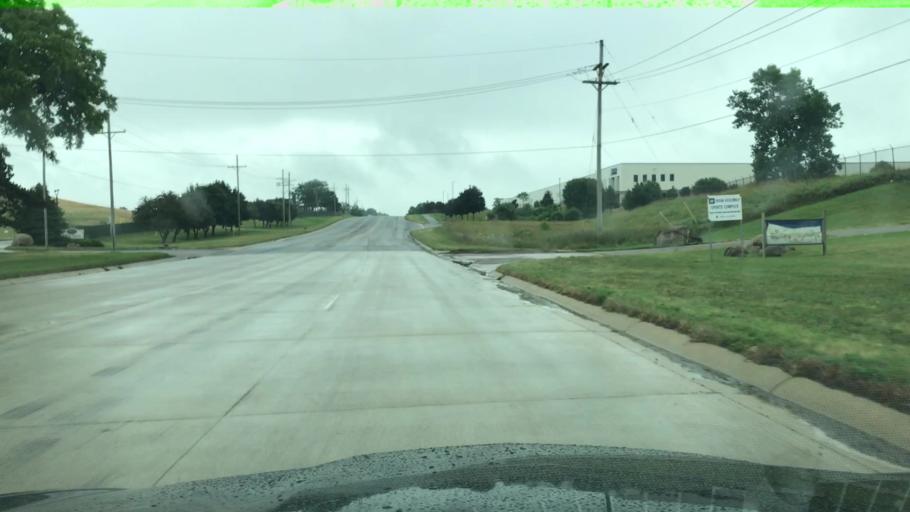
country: US
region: Michigan
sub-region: Oakland County
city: Auburn Hills
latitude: 42.7227
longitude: -83.2543
